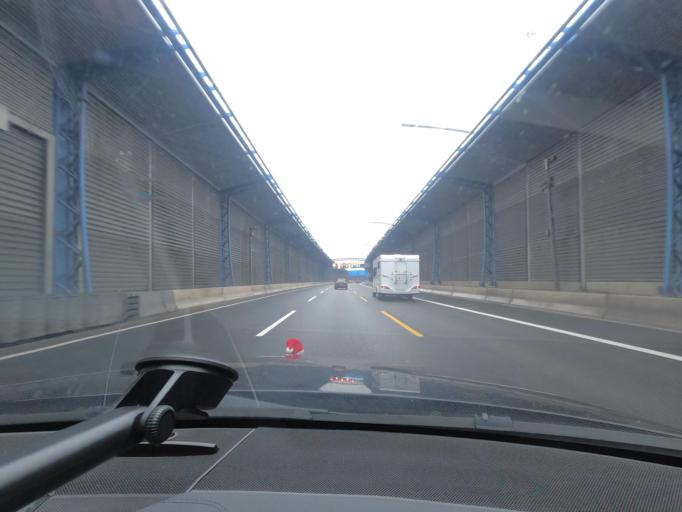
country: DE
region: Hamburg
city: Stellingen
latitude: 53.6294
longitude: 9.9376
